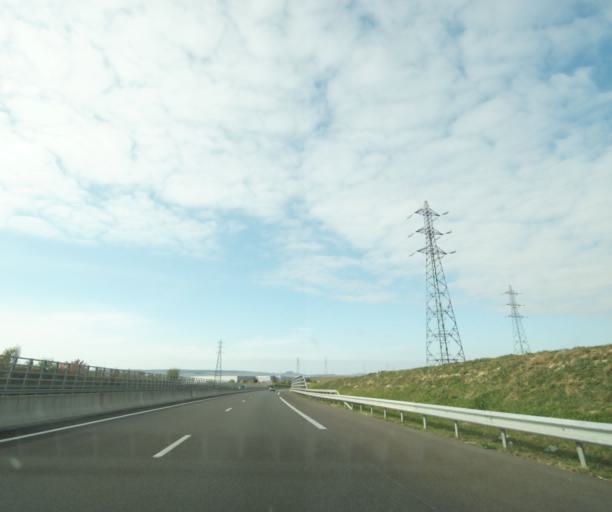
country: FR
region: Champagne-Ardenne
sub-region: Departement de la Marne
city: Cormontreuil
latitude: 49.2049
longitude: 4.0239
